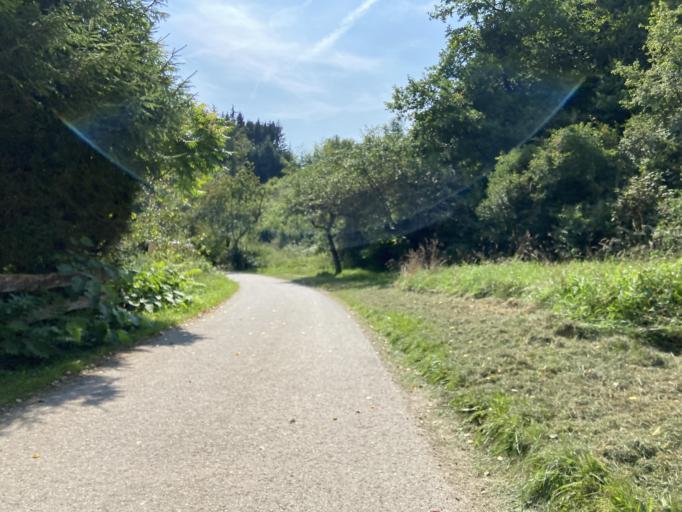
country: DE
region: Baden-Wuerttemberg
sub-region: Tuebingen Region
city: Bingen
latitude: 48.1022
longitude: 9.2864
